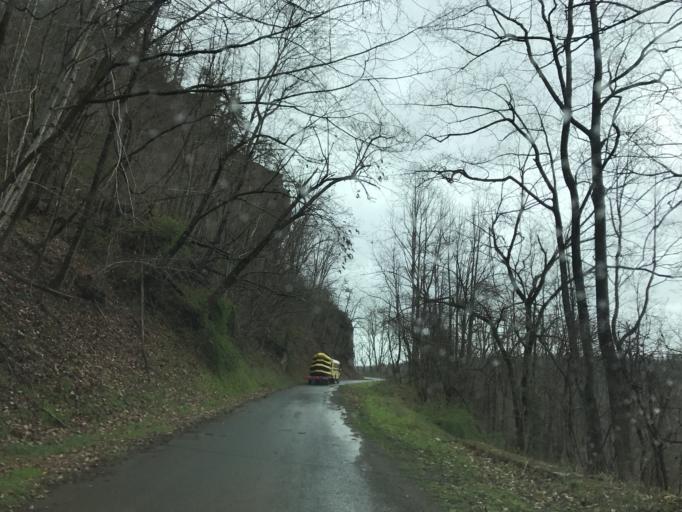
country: US
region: West Virginia
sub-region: Fayette County
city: Fayetteville
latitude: 38.0745
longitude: -81.0885
